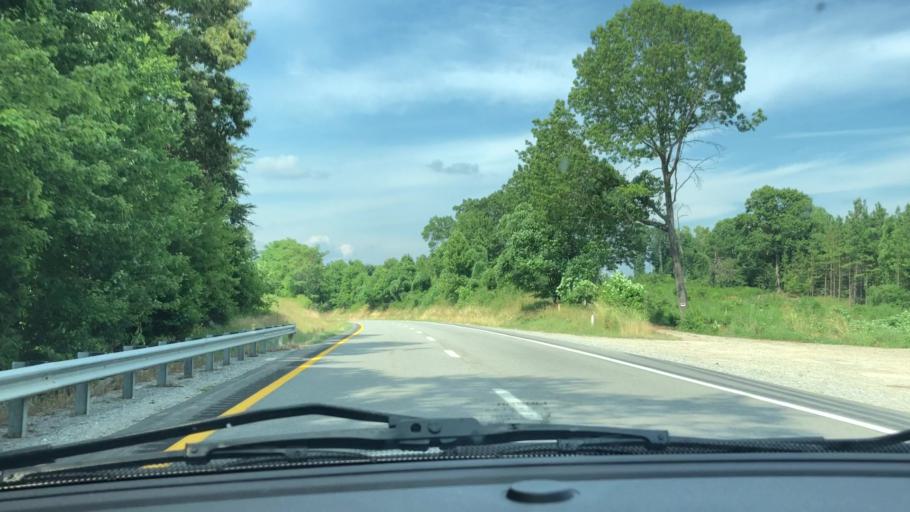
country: US
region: Virginia
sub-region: Henry County
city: Horse Pasture
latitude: 36.5661
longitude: -79.8757
